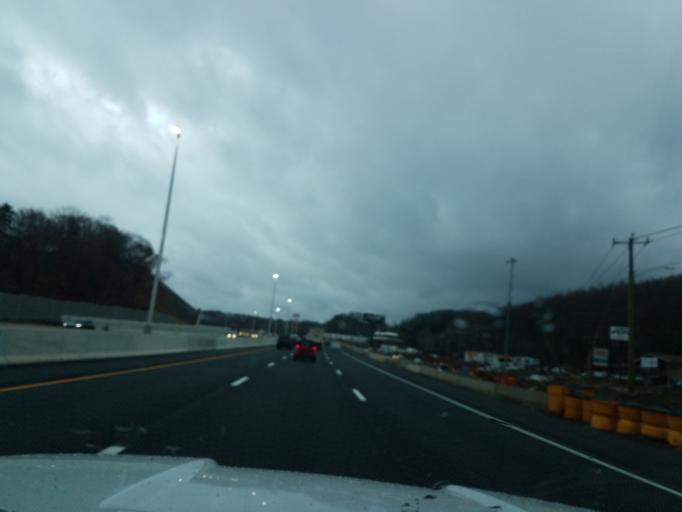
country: US
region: Connecticut
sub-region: New Haven County
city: Prospect
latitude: 41.5385
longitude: -73.0079
